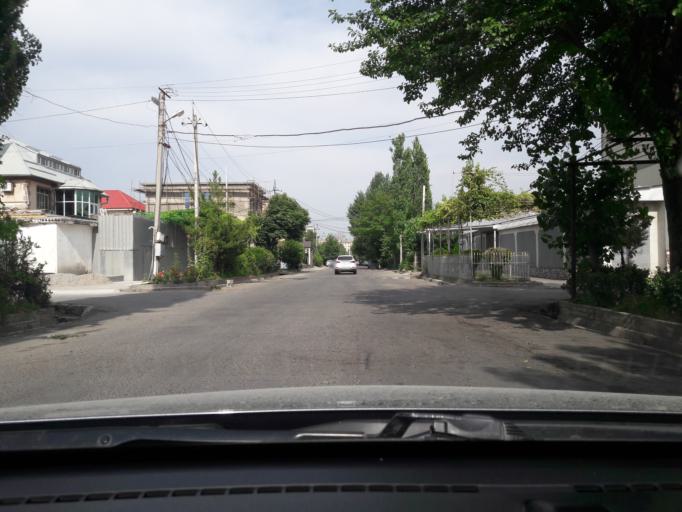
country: TJ
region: Dushanbe
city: Dushanbe
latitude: 38.5381
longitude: 68.7551
